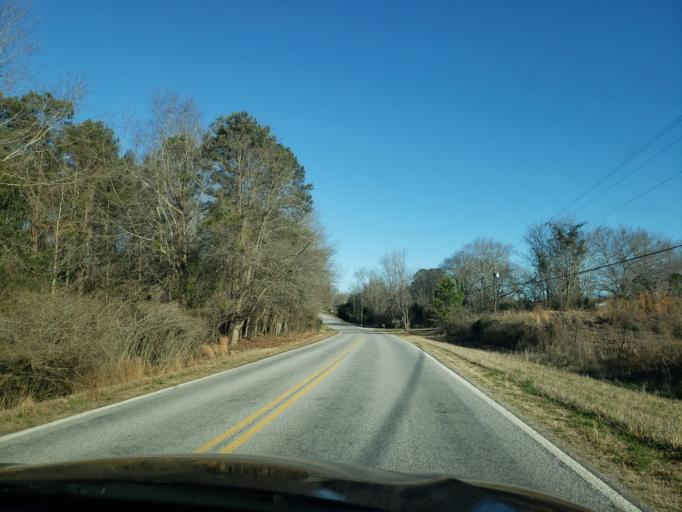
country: US
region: Alabama
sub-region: Elmore County
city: Tallassee
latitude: 32.5976
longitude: -85.8010
